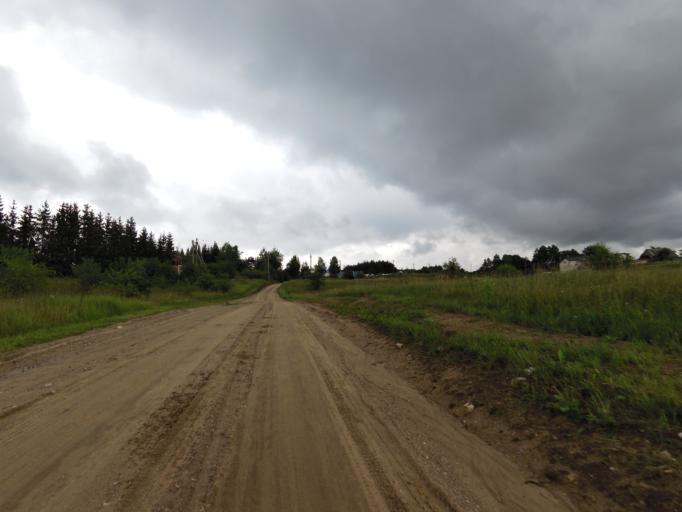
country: LT
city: Grigiskes
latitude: 54.7071
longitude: 25.1007
